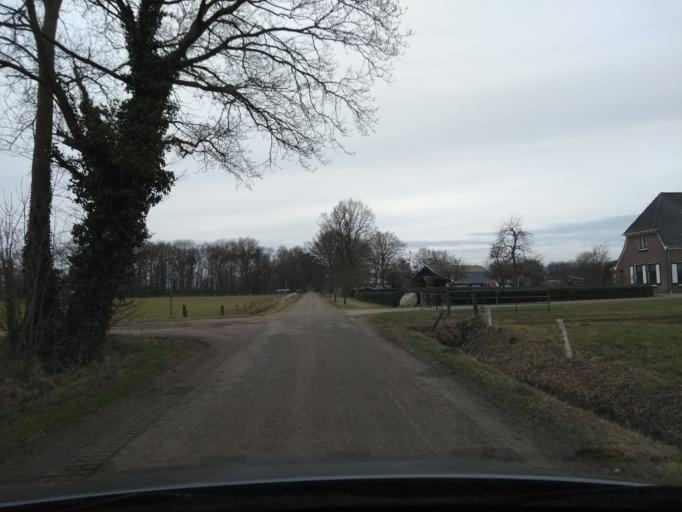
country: NL
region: Overijssel
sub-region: Gemeente Borne
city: Borne
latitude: 52.3313
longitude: 6.7364
